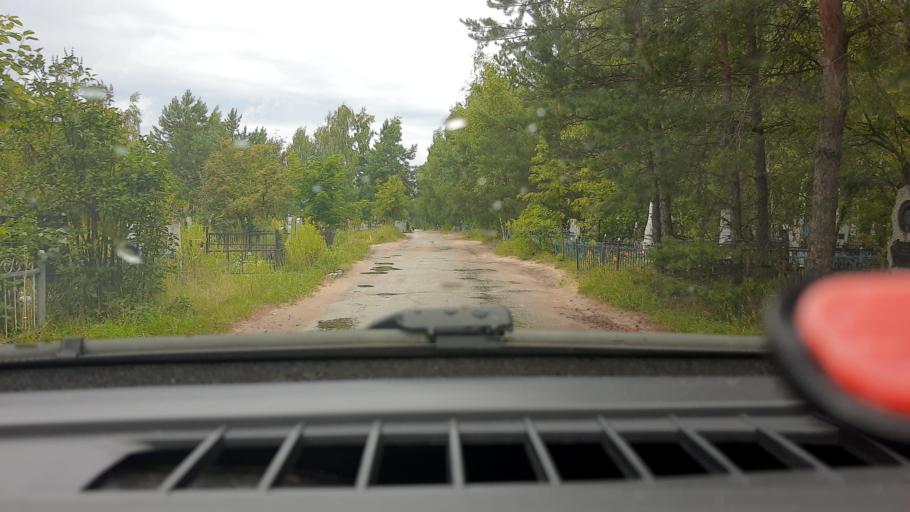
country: RU
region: Nizjnij Novgorod
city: Gorbatovka
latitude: 56.3529
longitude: 43.7775
